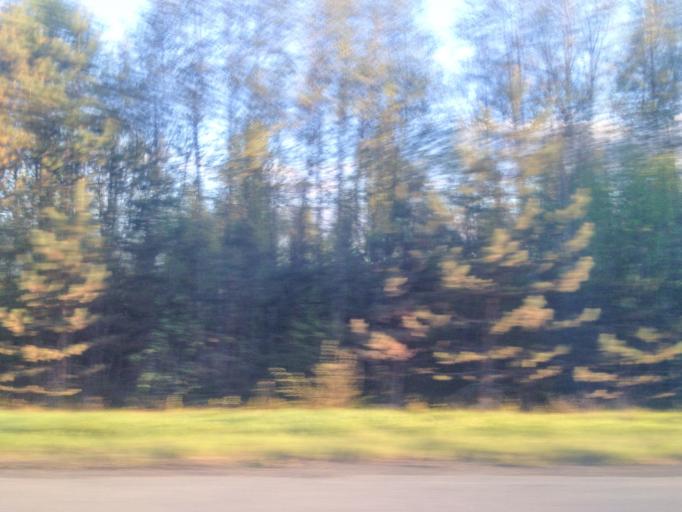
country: FI
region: Haeme
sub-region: Haemeenlinna
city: Parola
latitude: 61.0712
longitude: 24.2941
